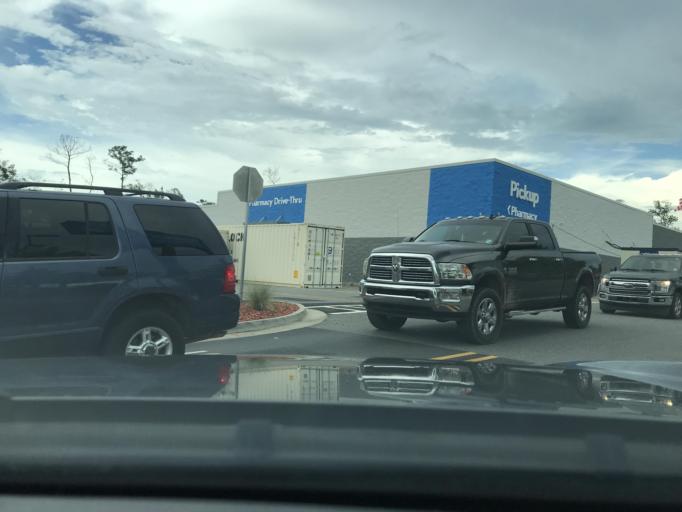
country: US
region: Louisiana
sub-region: Calcasieu Parish
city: Moss Bluff
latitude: 30.3018
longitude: -93.2000
